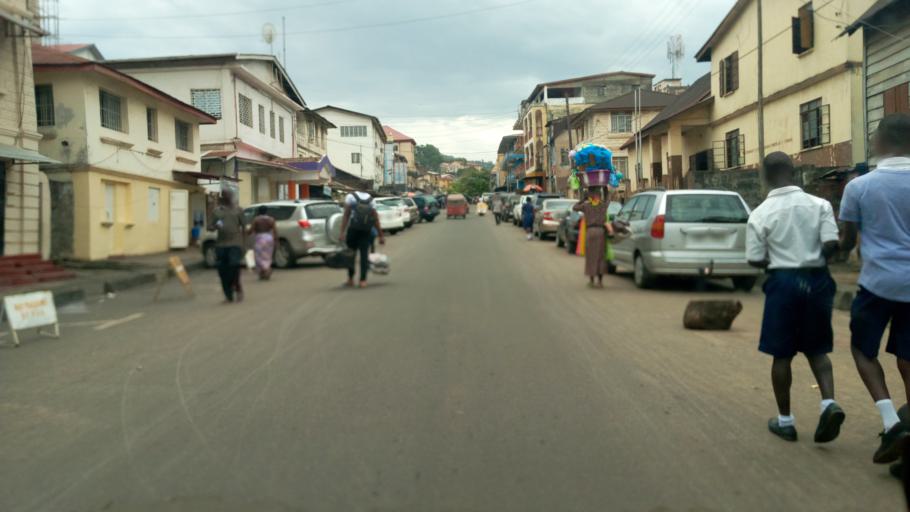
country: SL
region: Western Area
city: Freetown
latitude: 8.4860
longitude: -13.2380
